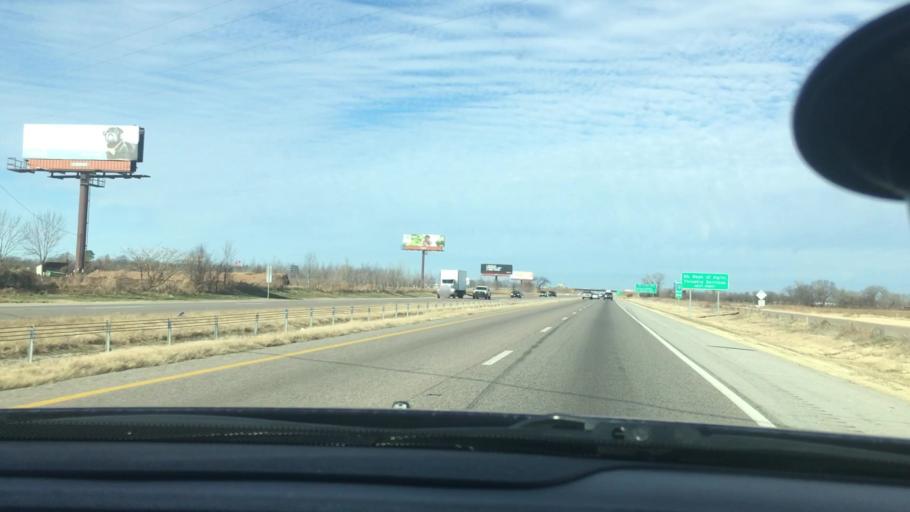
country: US
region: Oklahoma
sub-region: McClain County
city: Goldsby
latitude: 35.1460
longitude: -97.4700
